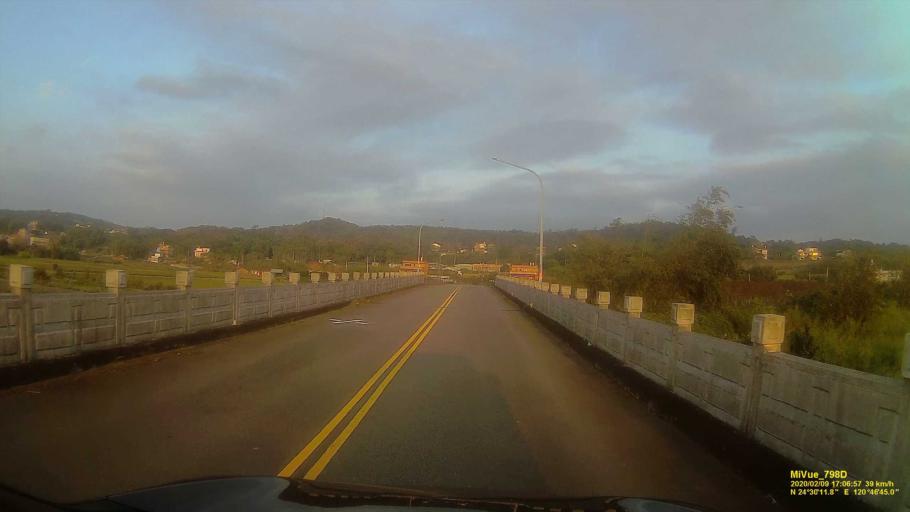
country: TW
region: Taiwan
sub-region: Miaoli
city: Miaoli
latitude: 24.5034
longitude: 120.7794
